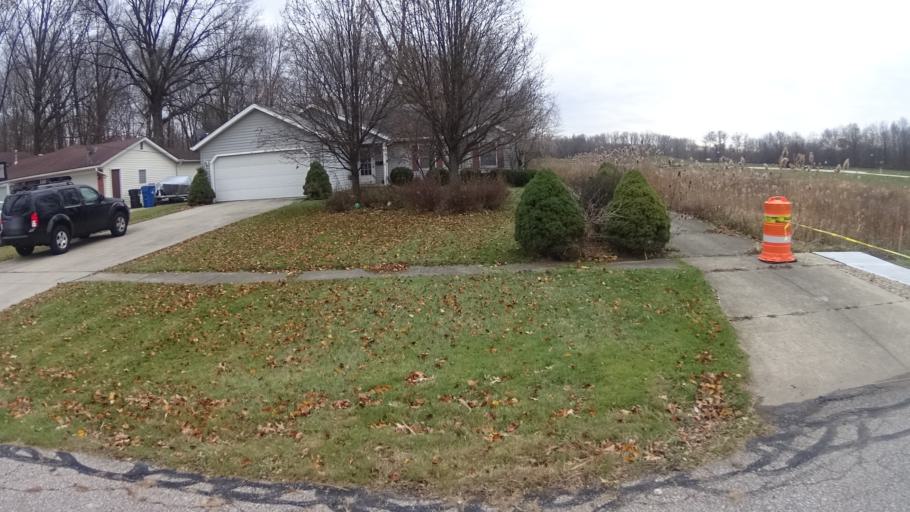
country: US
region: Ohio
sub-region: Lorain County
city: North Ridgeville
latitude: 41.3844
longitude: -82.0262
